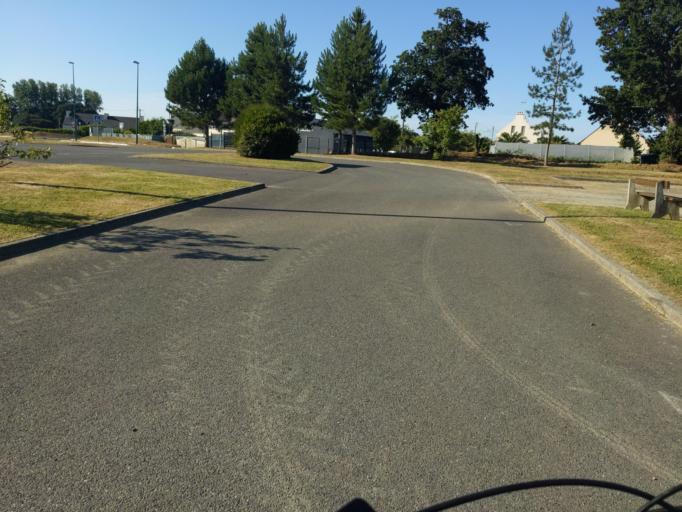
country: FR
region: Brittany
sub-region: Departement des Cotes-d'Armor
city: Pleubian
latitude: 48.8343
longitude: -3.1476
